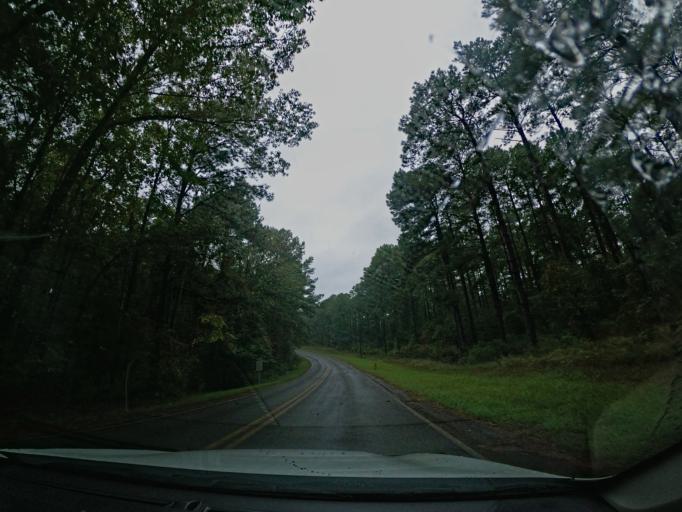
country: US
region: Louisiana
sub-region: Webster Parish
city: Minden
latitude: 32.6991
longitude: -93.2355
